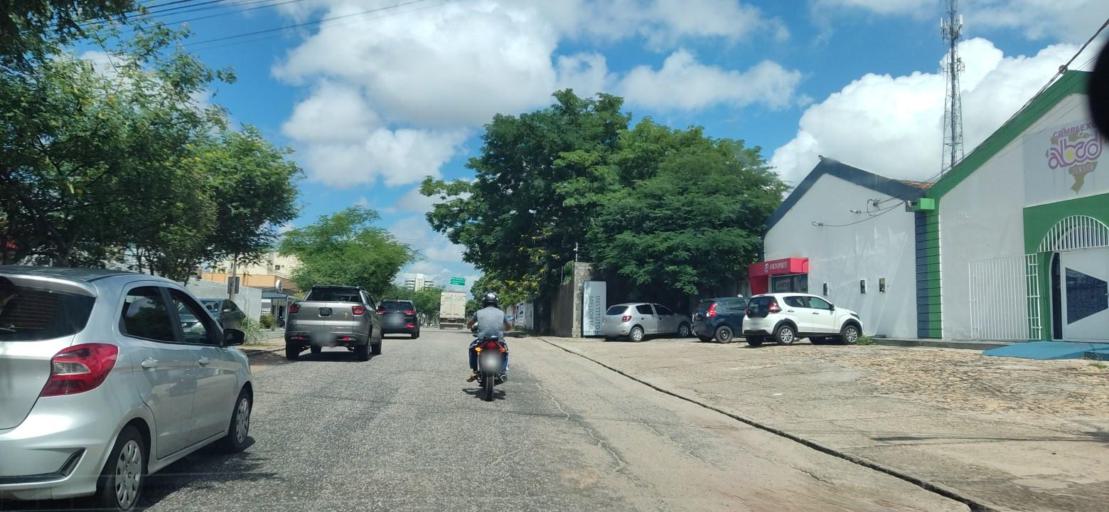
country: BR
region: Piaui
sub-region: Teresina
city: Teresina
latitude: -5.0705
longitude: -42.7692
